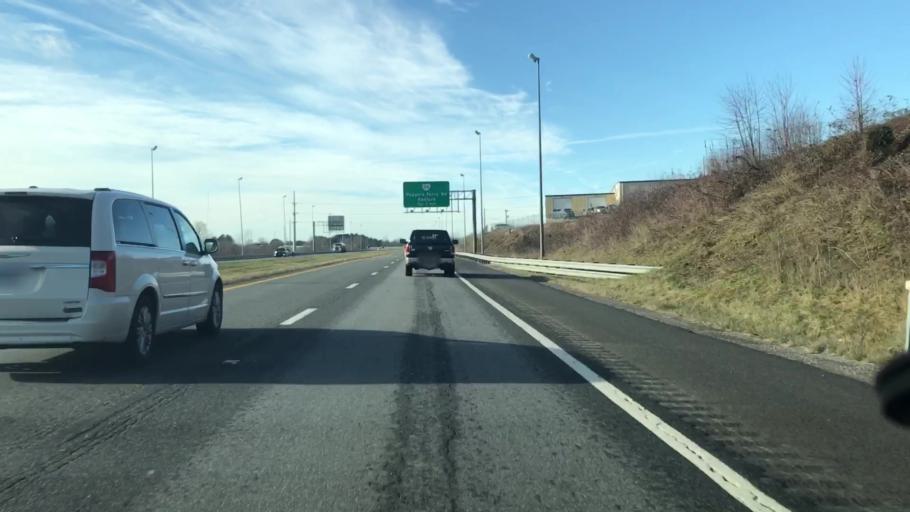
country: US
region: Virginia
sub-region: Montgomery County
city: Merrimac
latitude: 37.1793
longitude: -80.4098
